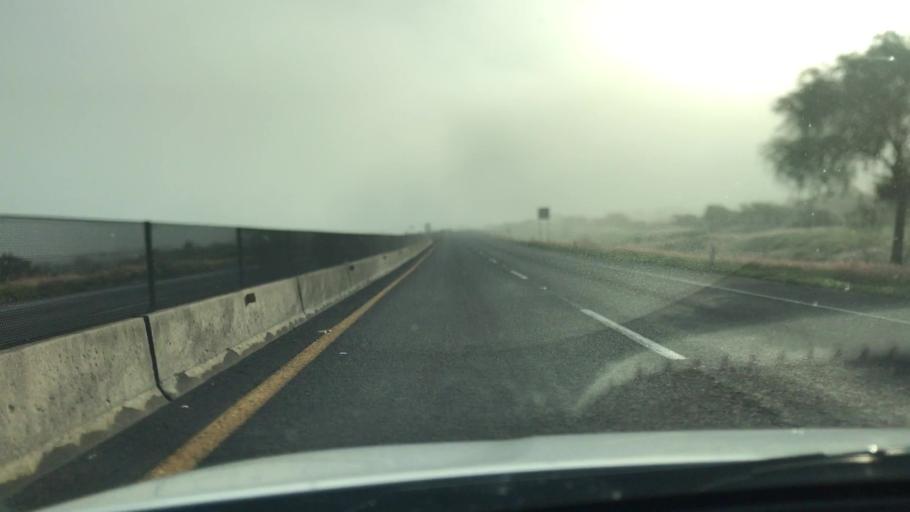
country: MX
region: Jalisco
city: Jalostotitlan
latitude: 21.0643
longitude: -102.5143
